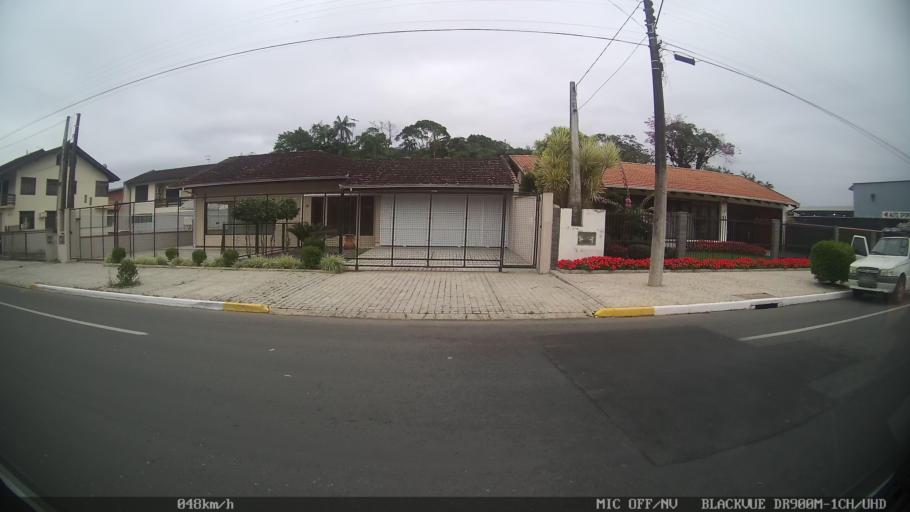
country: BR
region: Santa Catarina
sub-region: Joinville
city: Joinville
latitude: -26.2085
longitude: -48.9097
